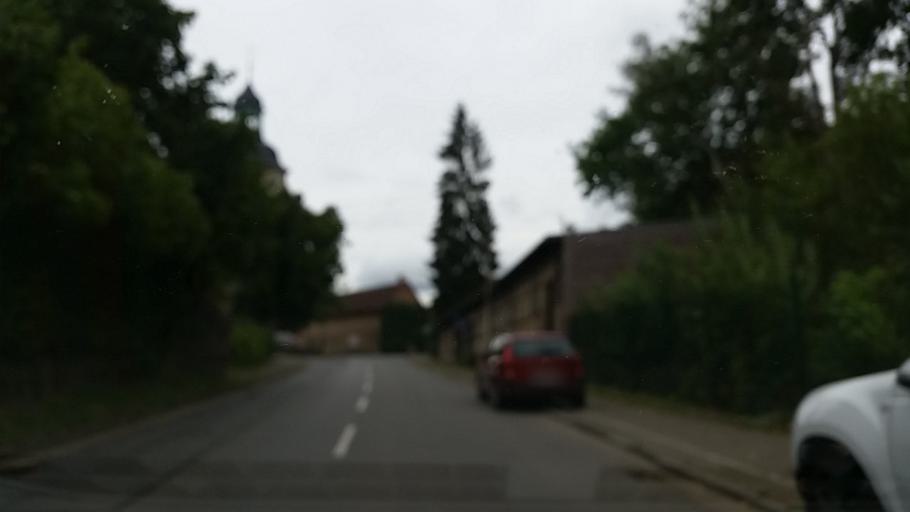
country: DE
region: Lower Saxony
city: Vienenburg
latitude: 51.9481
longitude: 10.5646
